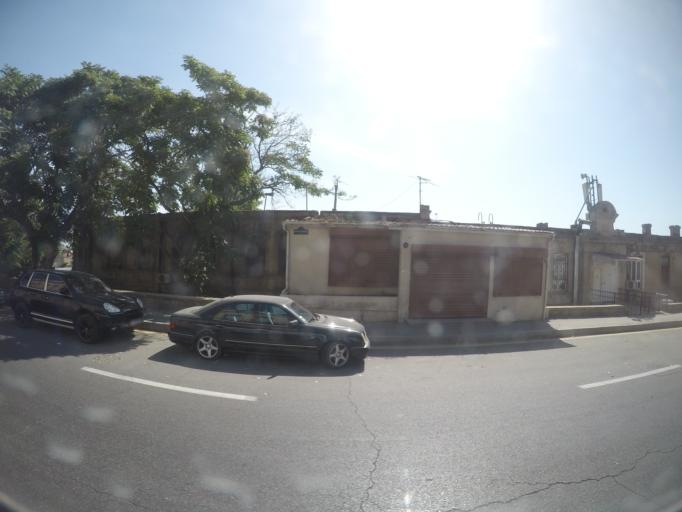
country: AZ
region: Baki
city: Badamdar
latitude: 40.3647
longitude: 49.8261
